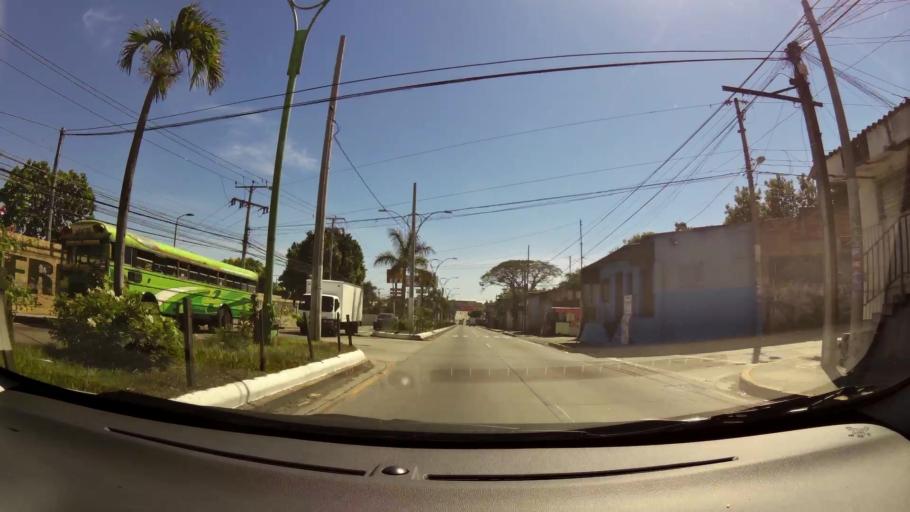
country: SV
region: San Salvador
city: Apopa
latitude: 13.7930
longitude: -89.1764
